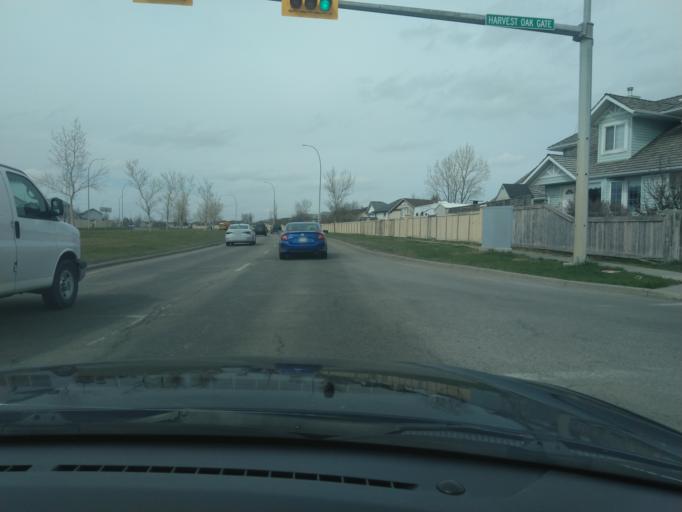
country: CA
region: Alberta
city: Calgary
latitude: 51.1470
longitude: -114.0635
